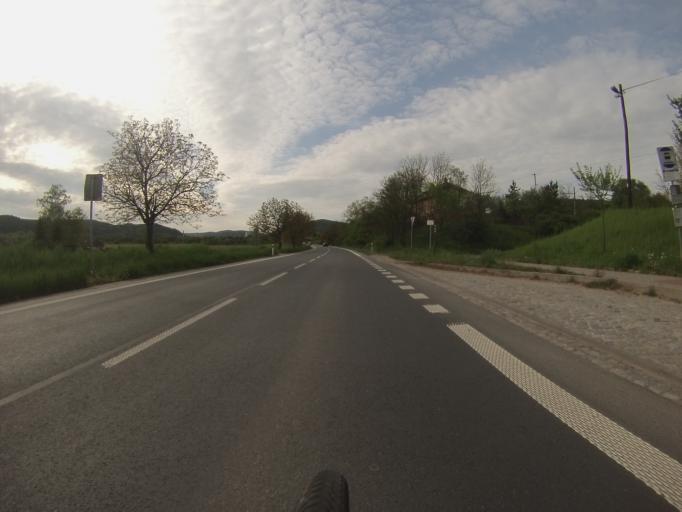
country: CZ
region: South Moravian
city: Tisnov
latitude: 49.3332
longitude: 16.4382
